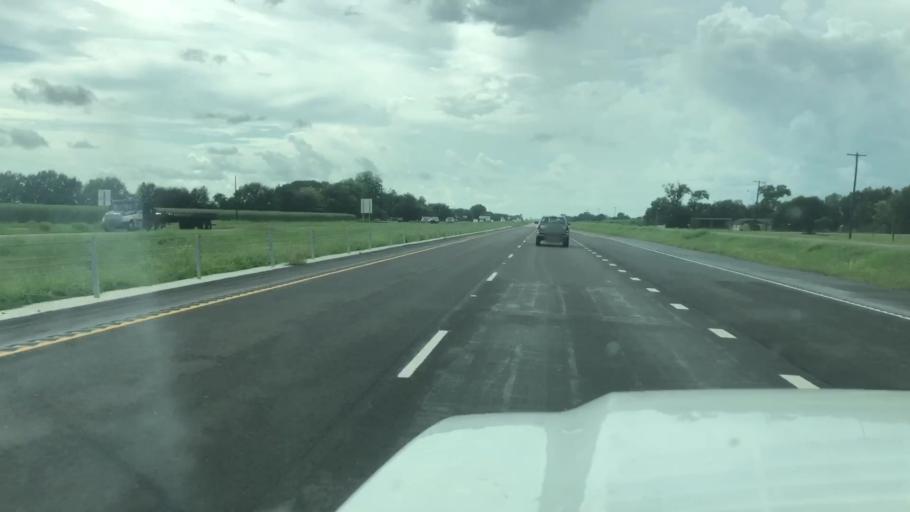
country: US
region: Louisiana
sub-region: Iberia Parish
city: Jeanerette
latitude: 29.8700
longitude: -91.6402
